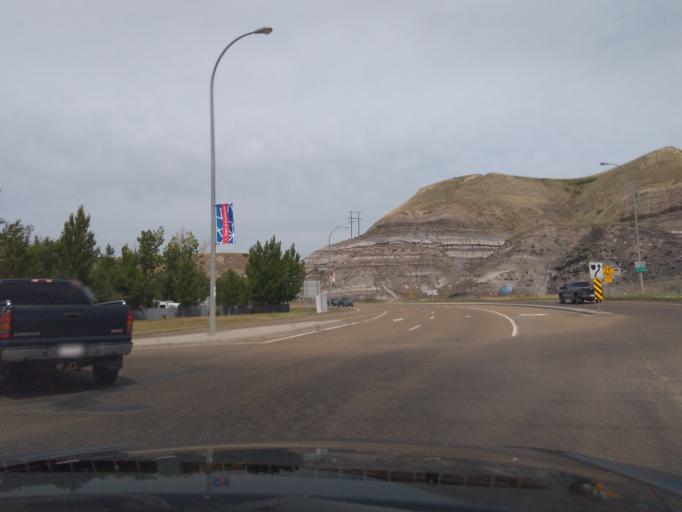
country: CA
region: Alberta
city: Three Hills
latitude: 51.4713
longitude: -112.7124
